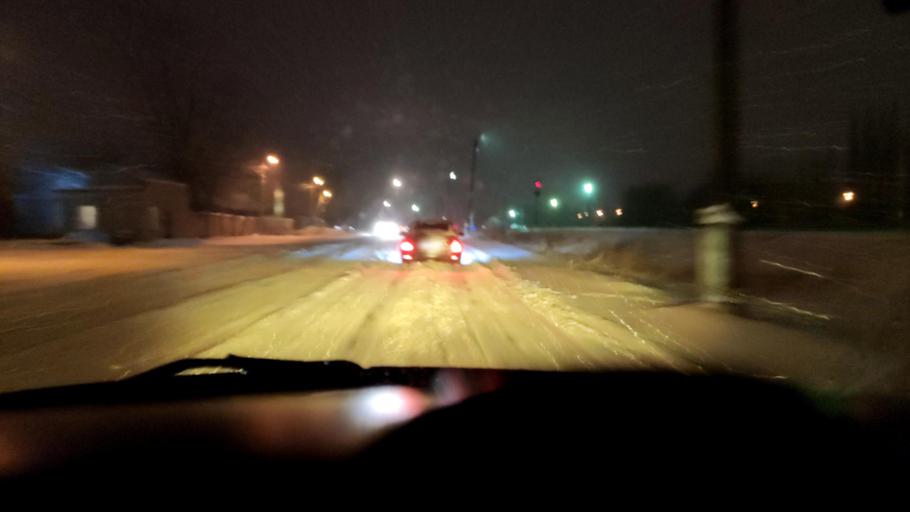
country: RU
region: Voronezj
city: Pridonskoy
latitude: 51.6814
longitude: 39.0704
